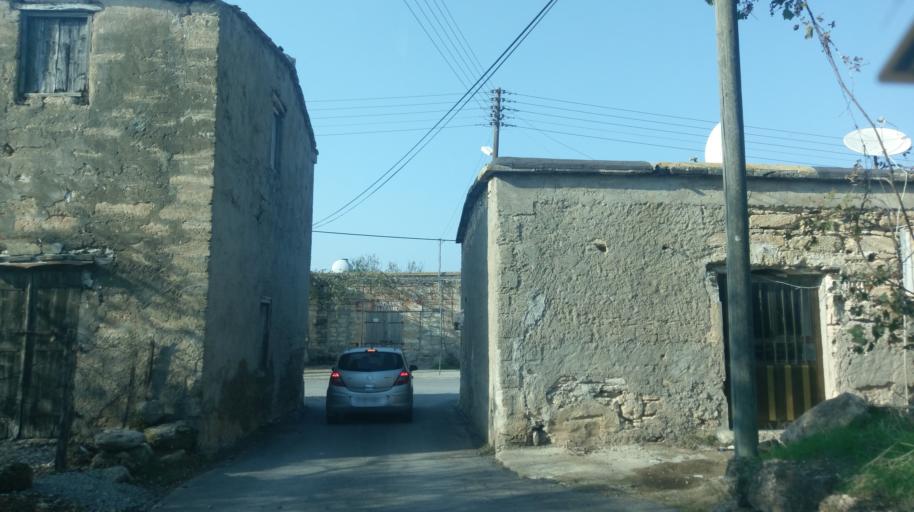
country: CY
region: Ammochostos
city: Leonarisso
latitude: 35.5389
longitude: 34.2158
